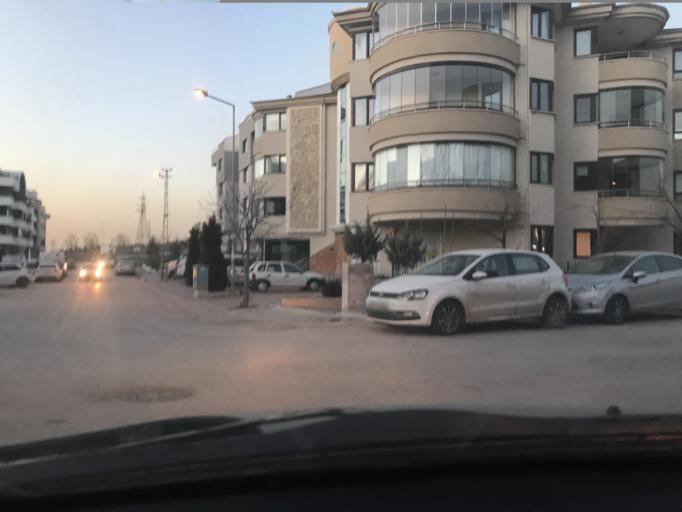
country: TR
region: Ankara
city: Batikent
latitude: 39.9146
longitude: 32.7727
